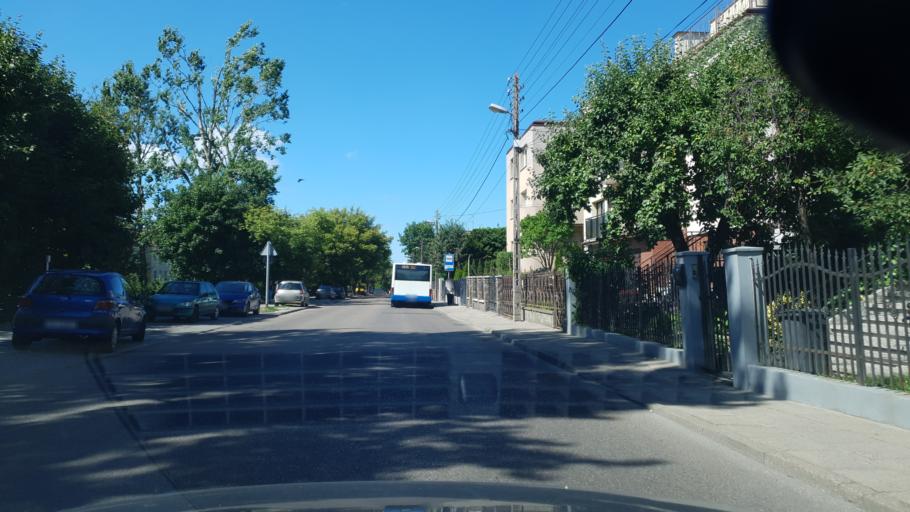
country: PL
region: Pomeranian Voivodeship
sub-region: Gdynia
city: Gdynia
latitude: 54.4993
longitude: 18.5418
